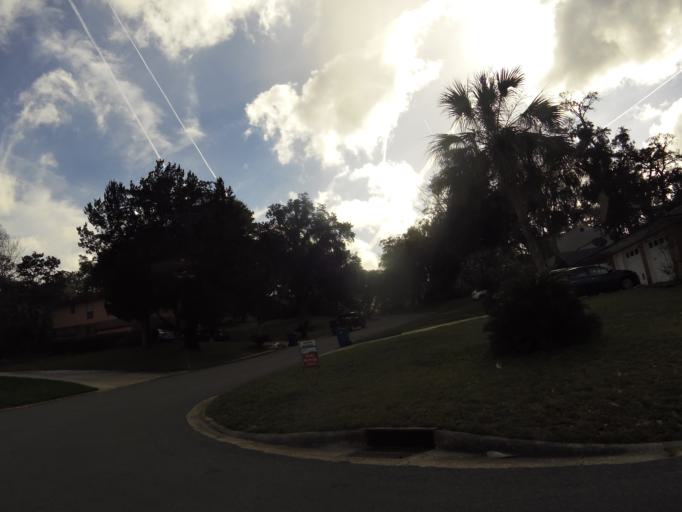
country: US
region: Florida
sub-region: Duval County
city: Atlantic Beach
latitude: 30.3767
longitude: -81.5125
